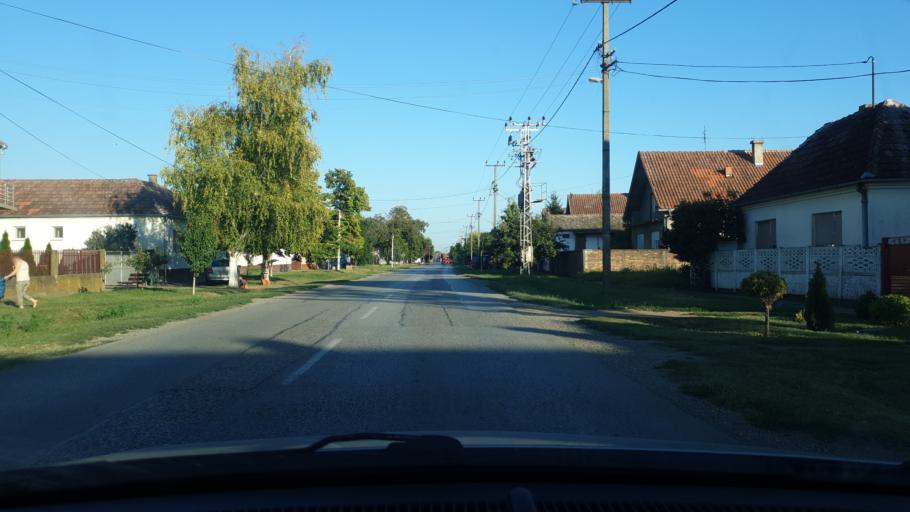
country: RS
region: Autonomna Pokrajina Vojvodina
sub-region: Sremski Okrug
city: Ruma
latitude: 44.9809
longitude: 19.8757
